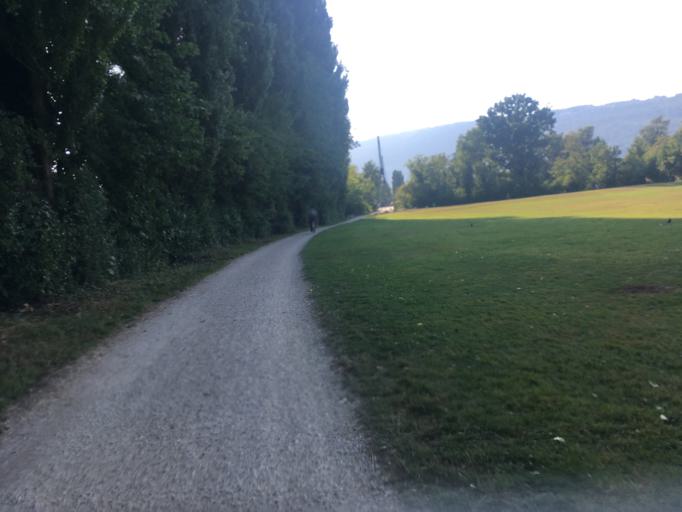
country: CH
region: Bern
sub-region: Biel/Bienne District
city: Bellmund
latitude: 47.1195
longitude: 7.2566
